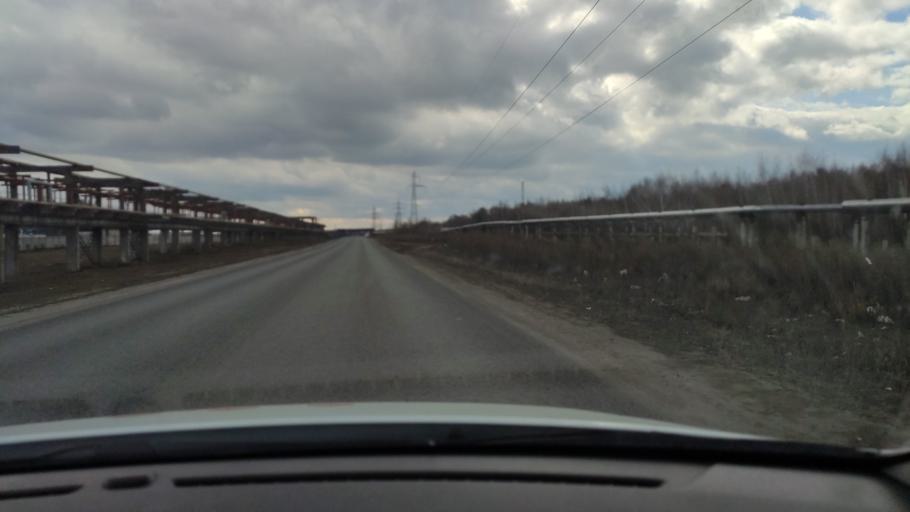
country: RU
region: Tatarstan
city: Staroye Arakchino
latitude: 55.8762
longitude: 48.9752
